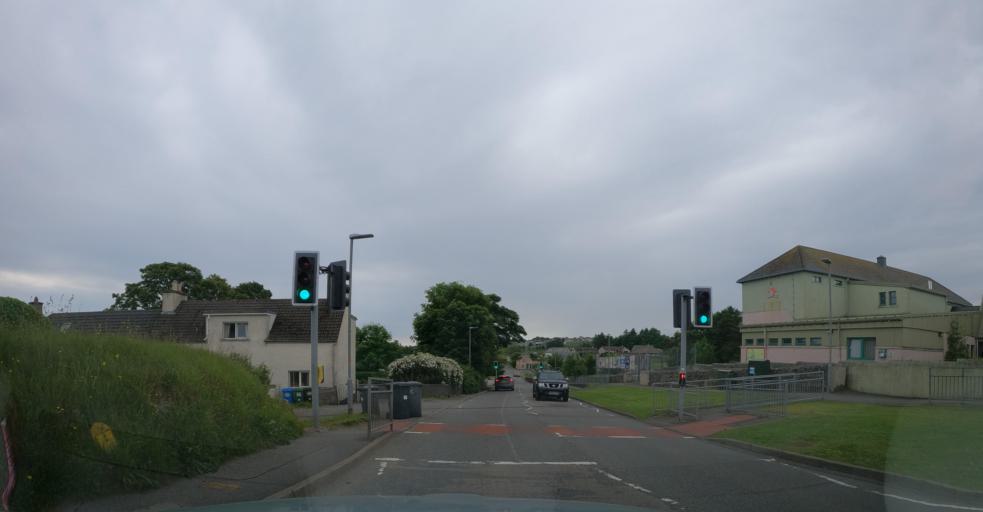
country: GB
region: Scotland
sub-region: Eilean Siar
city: Isle of Lewis
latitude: 58.2295
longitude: -6.3893
